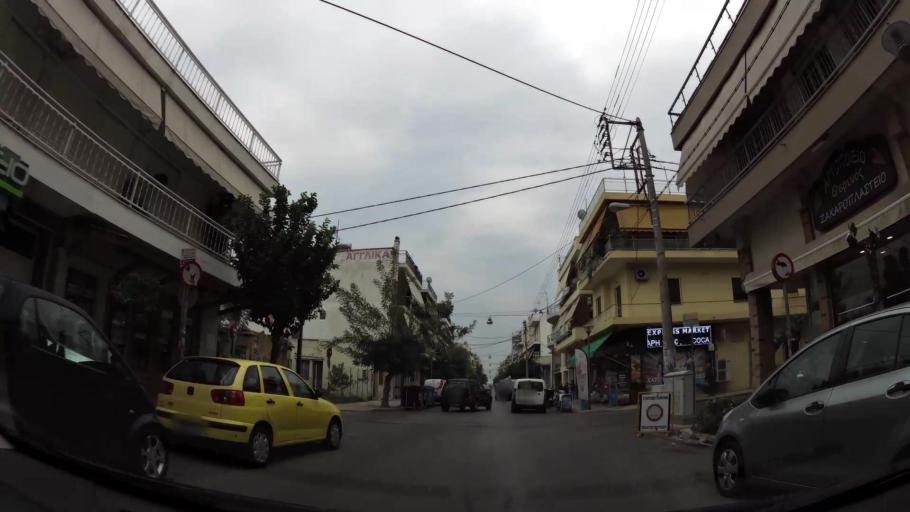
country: GR
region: Attica
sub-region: Nomarchia Athinas
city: Aigaleo
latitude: 37.9897
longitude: 23.6816
